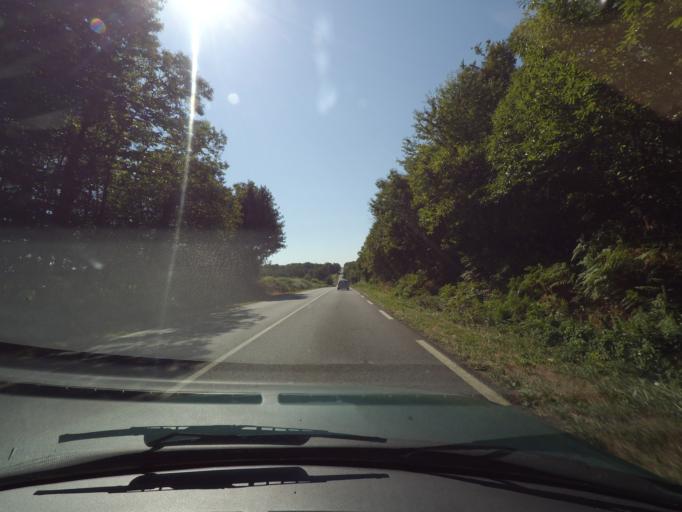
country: FR
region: Limousin
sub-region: Departement de la Haute-Vienne
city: Bussiere-Poitevine
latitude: 46.1806
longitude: 0.9390
